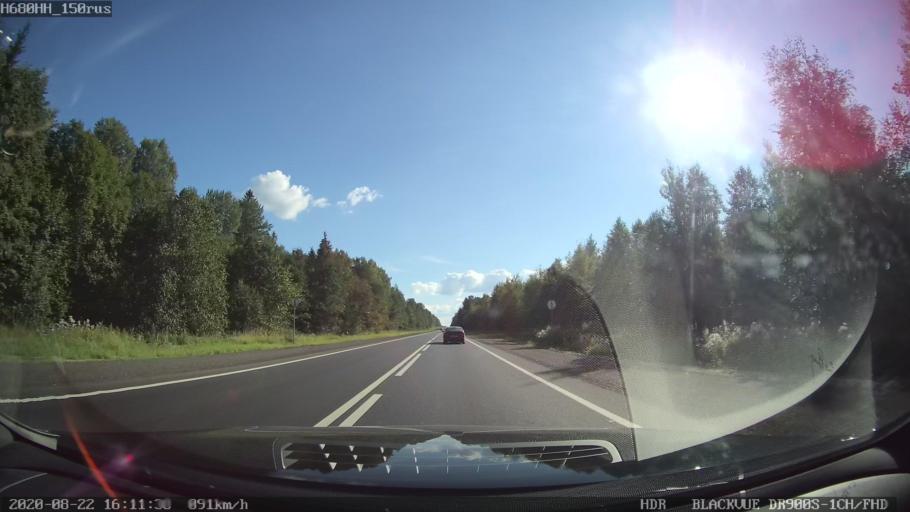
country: RU
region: Tverskaya
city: Rameshki
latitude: 57.4993
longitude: 36.2583
